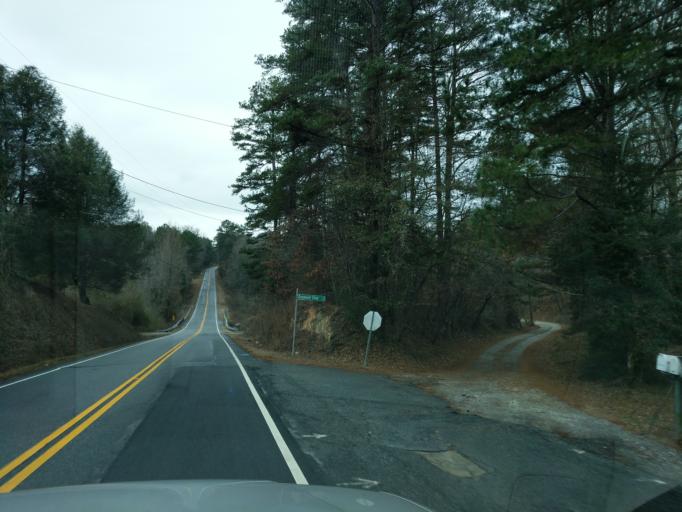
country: US
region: South Carolina
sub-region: Oconee County
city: Walhalla
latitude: 34.8147
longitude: -83.0473
